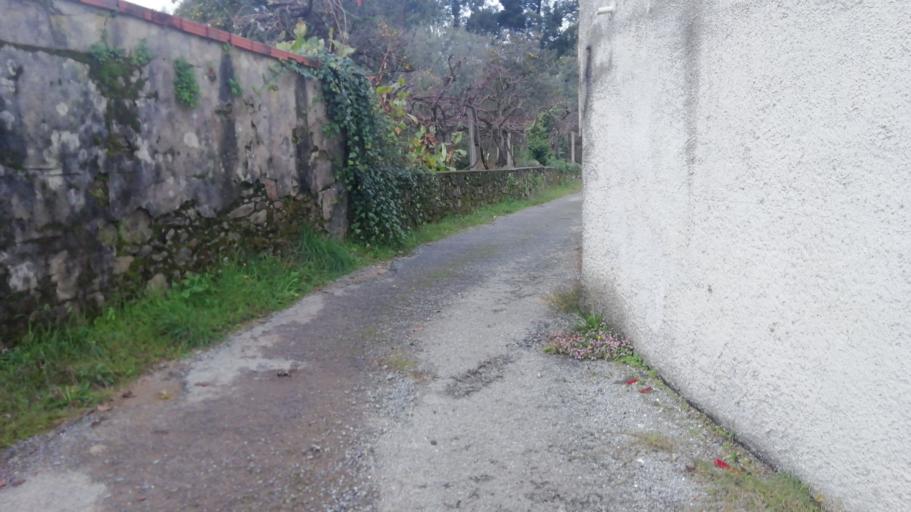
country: PT
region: Braga
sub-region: Vila Verde
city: Prado
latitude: 41.6536
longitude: -8.5121
